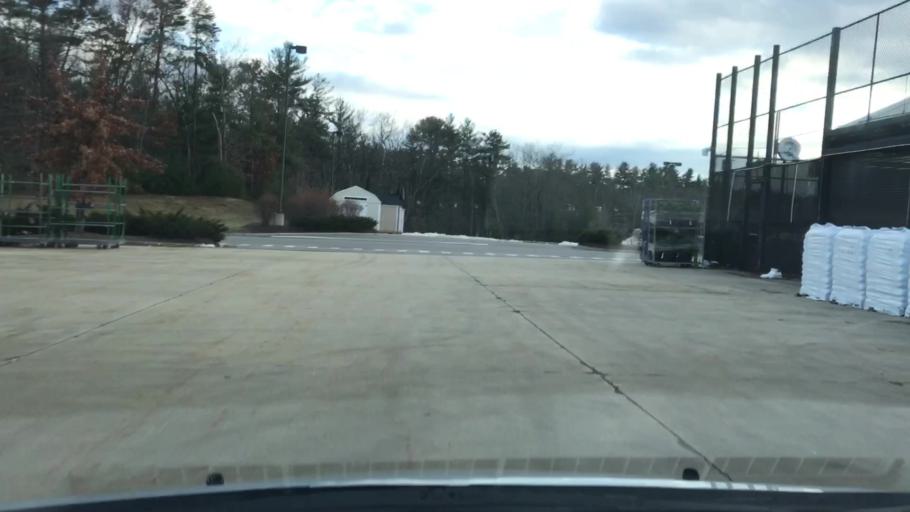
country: US
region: New Hampshire
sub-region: Merrimack County
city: South Hooksett
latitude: 43.0441
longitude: -71.4592
